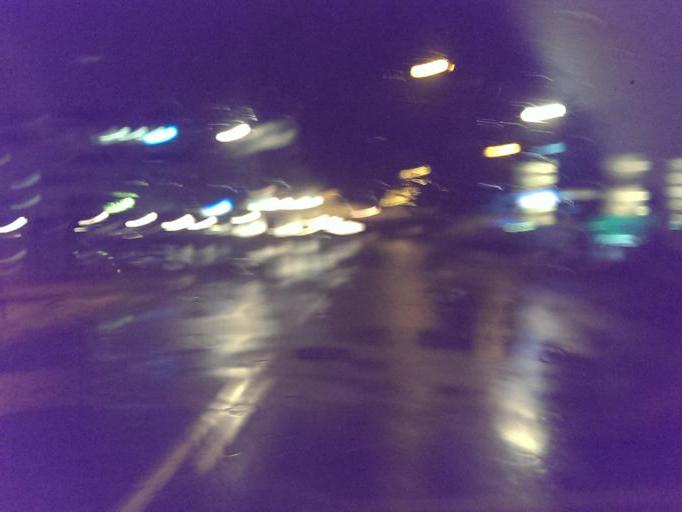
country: DK
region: South Denmark
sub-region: Esbjerg Kommune
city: Esbjerg
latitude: 55.4626
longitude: 8.4469
